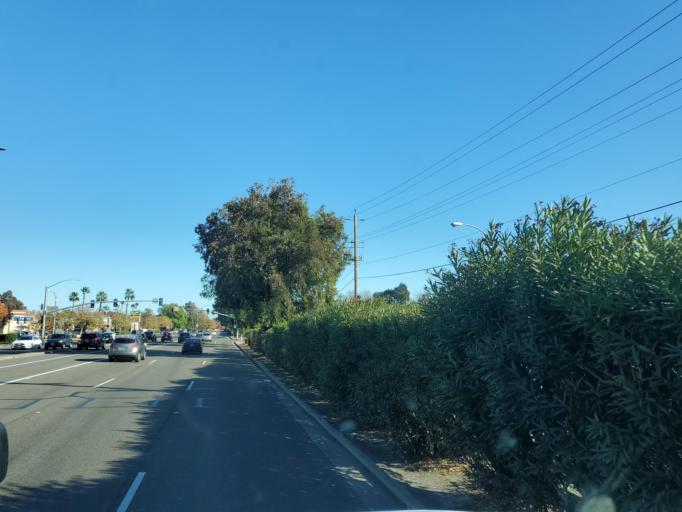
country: US
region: California
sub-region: San Joaquin County
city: Lincoln Village
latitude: 38.0212
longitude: -121.3468
